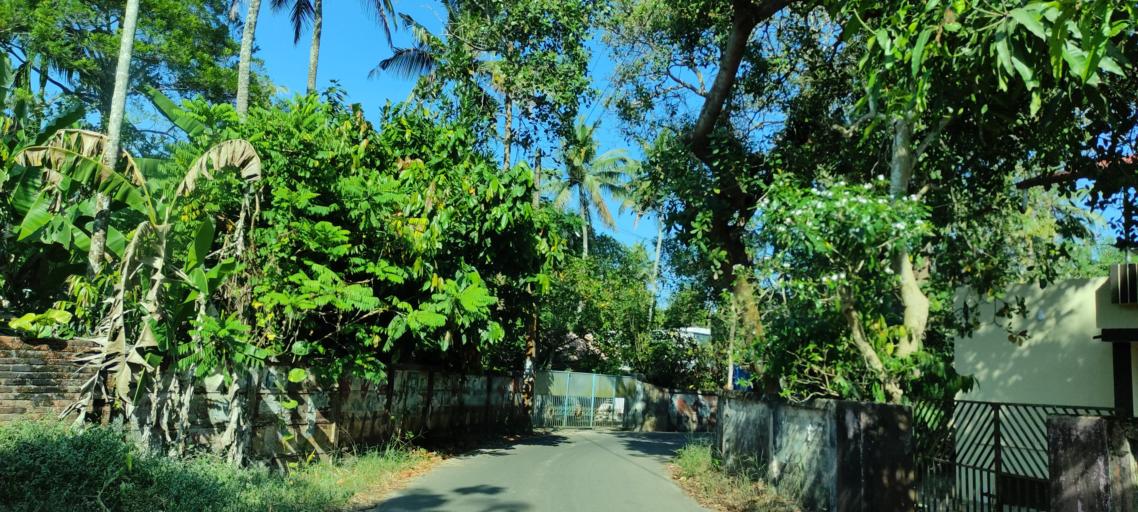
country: IN
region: Kerala
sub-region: Alappuzha
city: Alleppey
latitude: 9.5675
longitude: 76.3292
